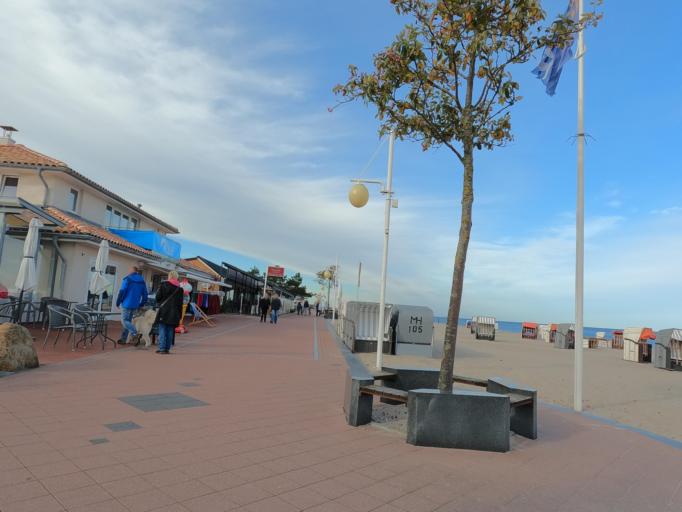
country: DE
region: Schleswig-Holstein
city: Dahme
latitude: 54.2271
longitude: 11.0872
